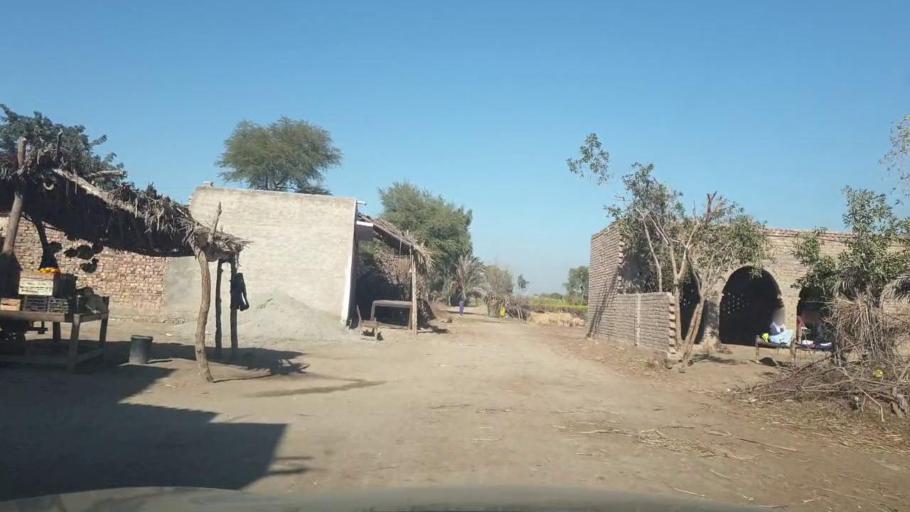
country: PK
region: Sindh
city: Mirpur Mathelo
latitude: 28.0815
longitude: 69.4893
